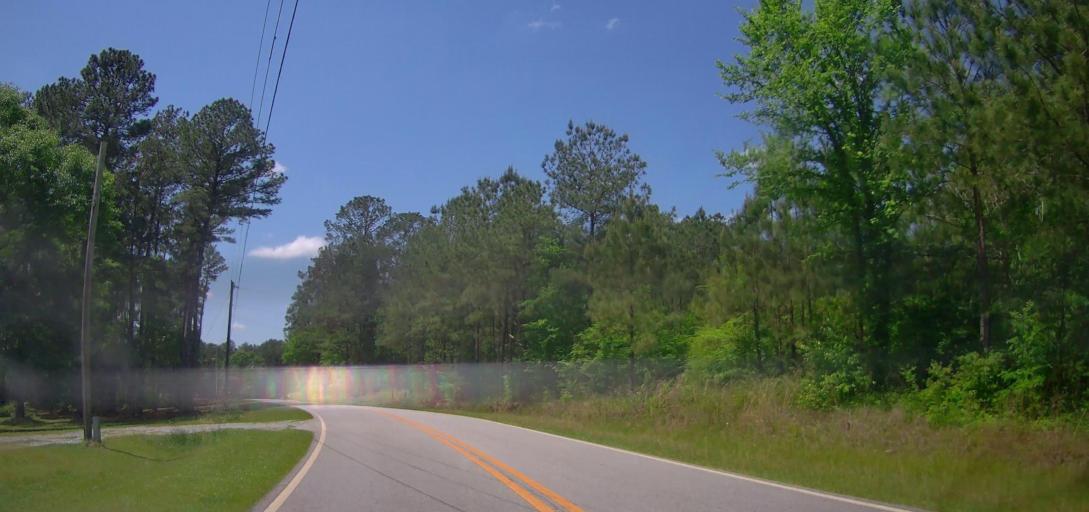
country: US
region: Georgia
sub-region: Bibb County
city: Macon
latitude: 32.9259
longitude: -83.5940
